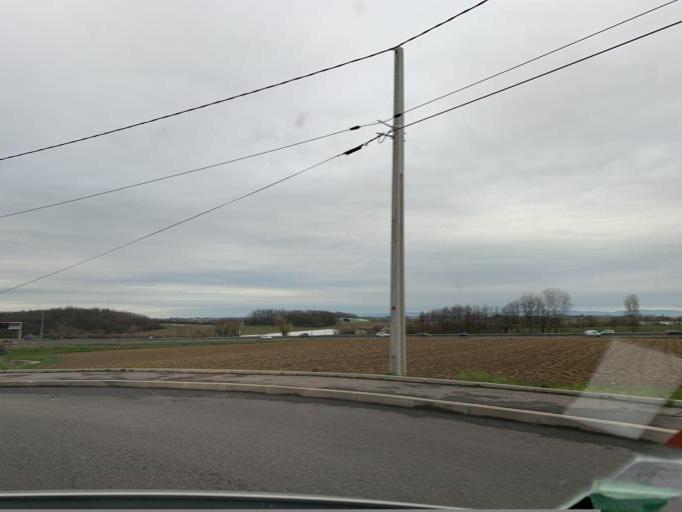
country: FR
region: Rhone-Alpes
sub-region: Departement du Rhone
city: Rillieux-la-Pape
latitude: 45.8377
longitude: 4.9147
